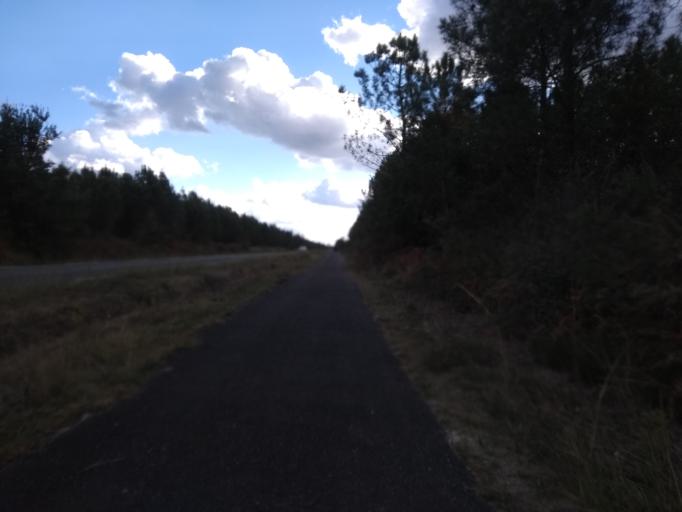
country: FR
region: Aquitaine
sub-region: Departement de la Gironde
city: Cestas
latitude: 44.7257
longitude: -0.6891
